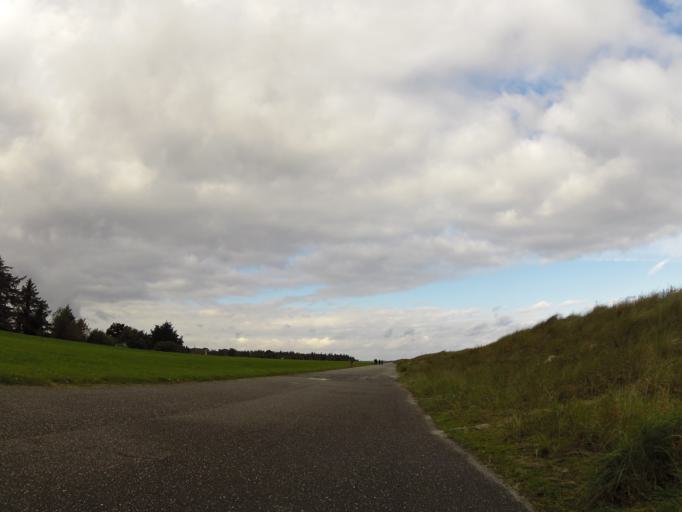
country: DE
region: Schleswig-Holstein
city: Wisch
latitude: 54.4317
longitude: 10.3547
